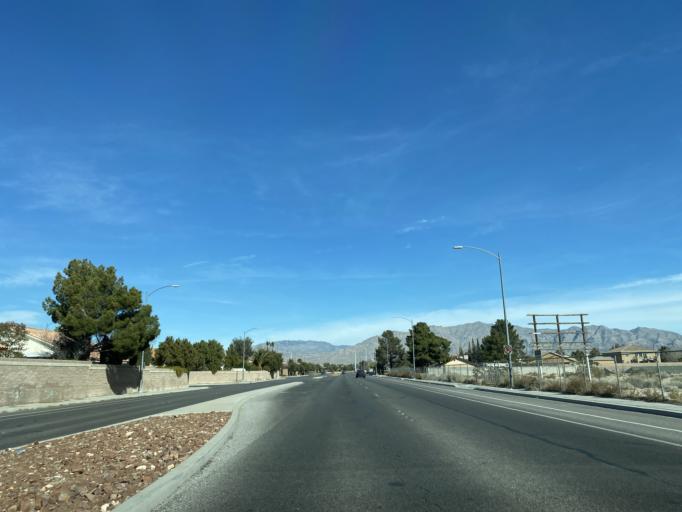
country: US
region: Nevada
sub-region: Clark County
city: Las Vegas
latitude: 36.2632
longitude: -115.2254
